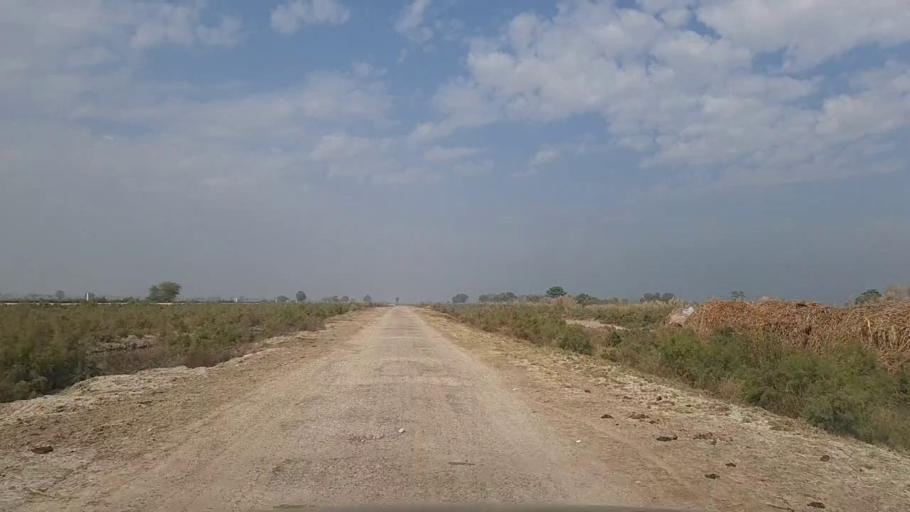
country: PK
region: Sindh
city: Daur
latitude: 26.3916
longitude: 68.3499
